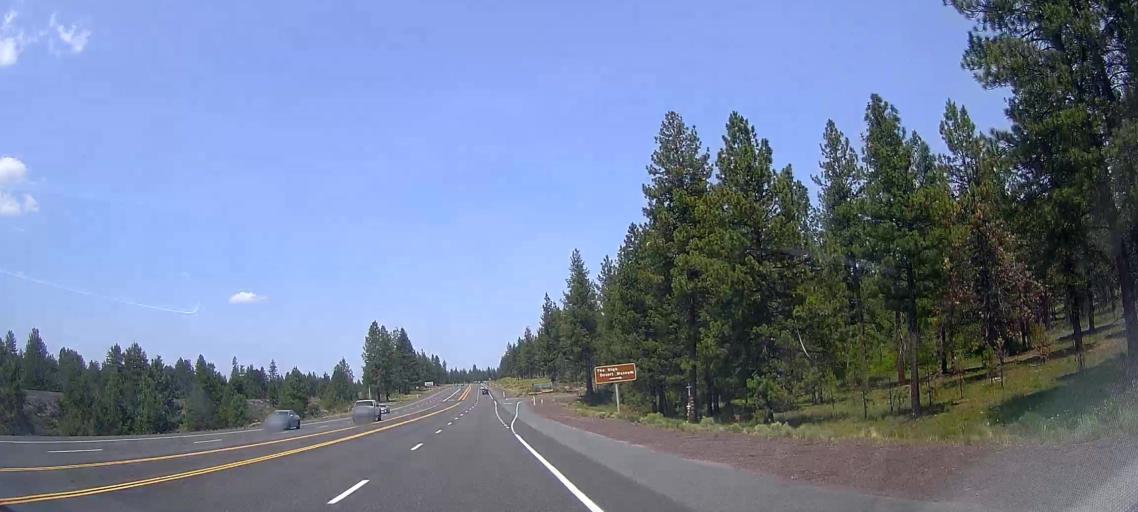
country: US
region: Oregon
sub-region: Deschutes County
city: Deschutes River Woods
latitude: 43.9694
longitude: -121.3466
